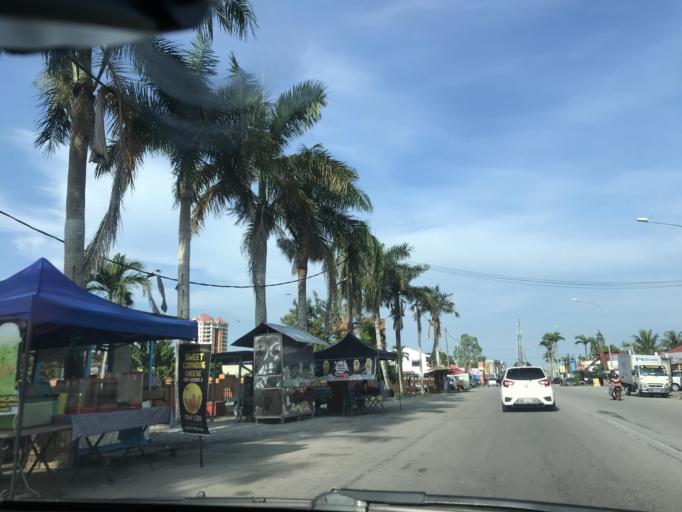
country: MY
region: Kelantan
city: Kota Bharu
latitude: 6.1195
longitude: 102.2887
